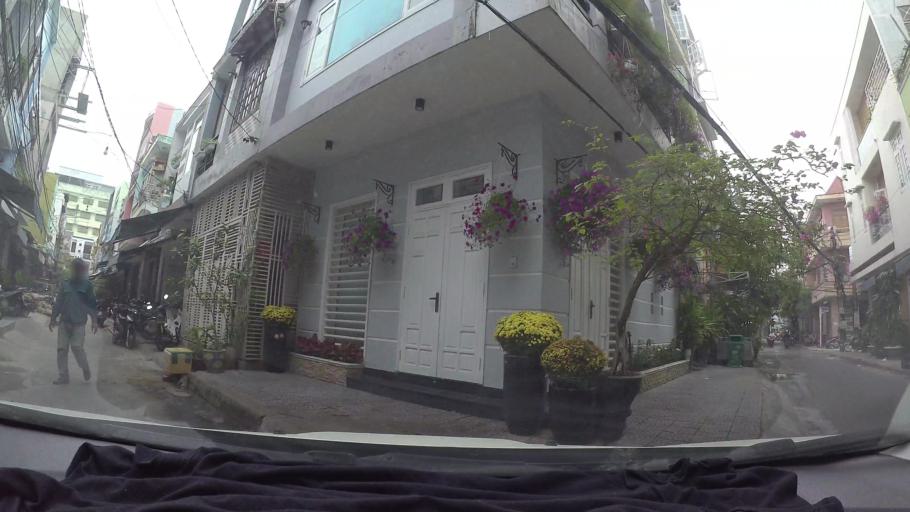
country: VN
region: Da Nang
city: Da Nang
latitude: 16.0579
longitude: 108.2120
